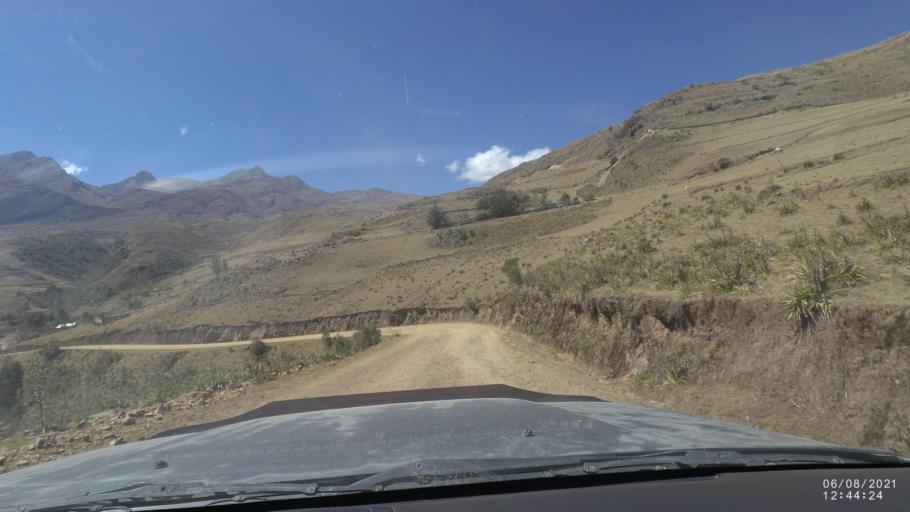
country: BO
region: Cochabamba
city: Colchani
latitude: -16.7691
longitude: -66.6661
